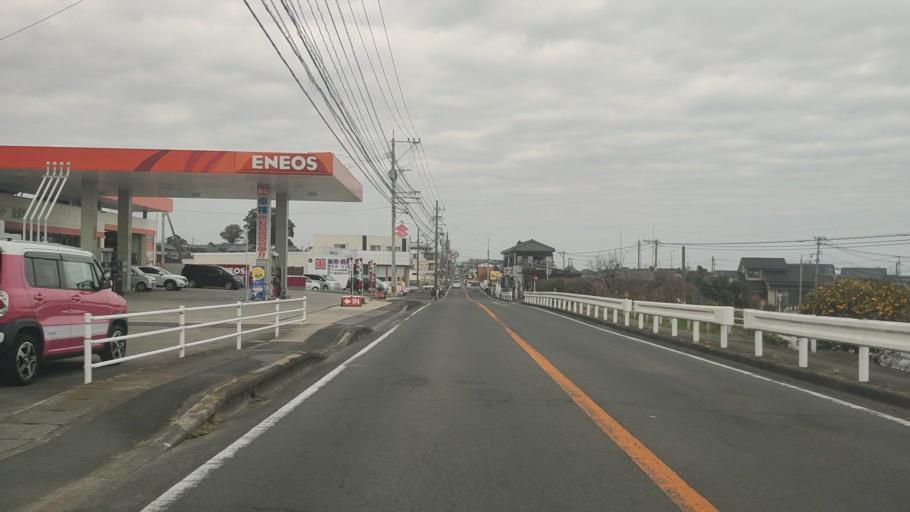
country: JP
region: Nagasaki
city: Shimabara
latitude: 32.8225
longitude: 130.3533
